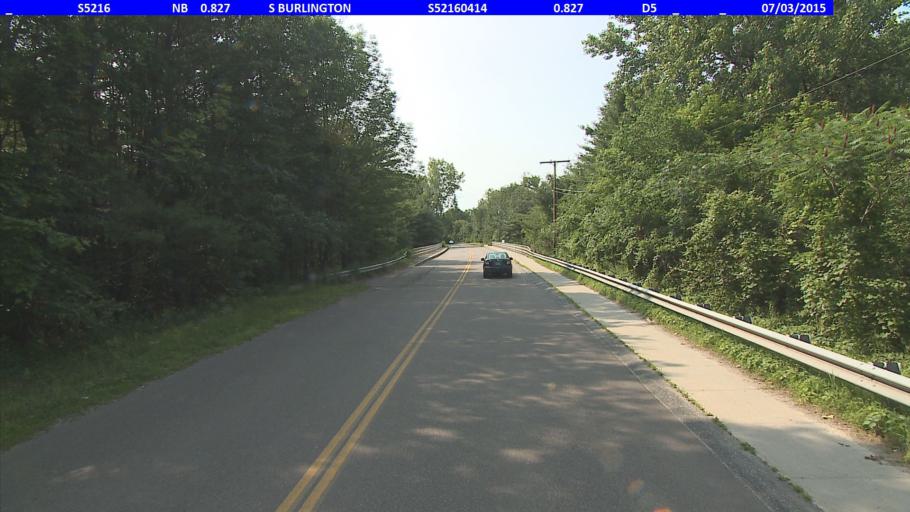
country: US
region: Vermont
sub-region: Chittenden County
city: South Burlington
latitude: 44.4780
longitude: -73.1759
